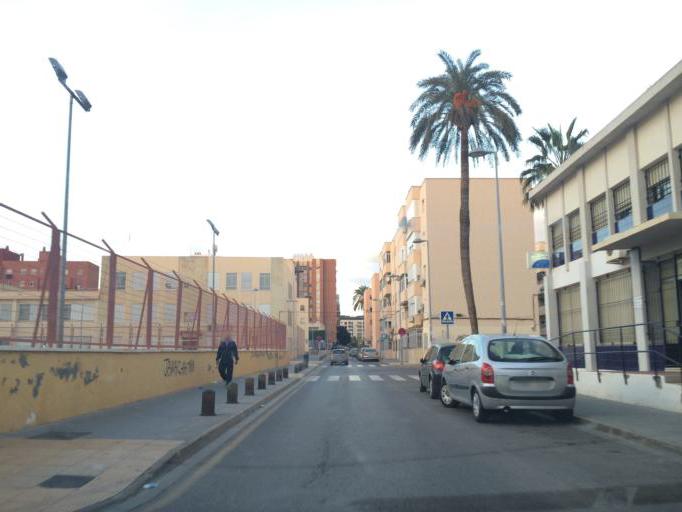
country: ES
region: Andalusia
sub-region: Provincia de Almeria
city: Almeria
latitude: 36.8329
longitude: -2.4491
